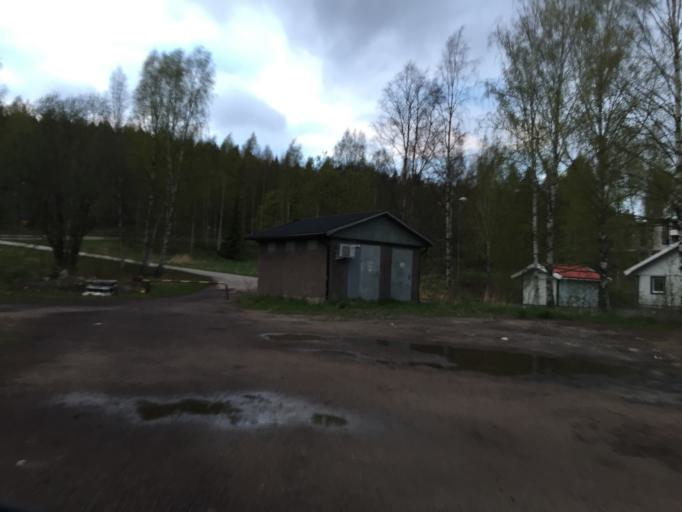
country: SE
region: Dalarna
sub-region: Ludvika Kommun
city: Ludvika
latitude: 60.1365
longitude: 15.2012
